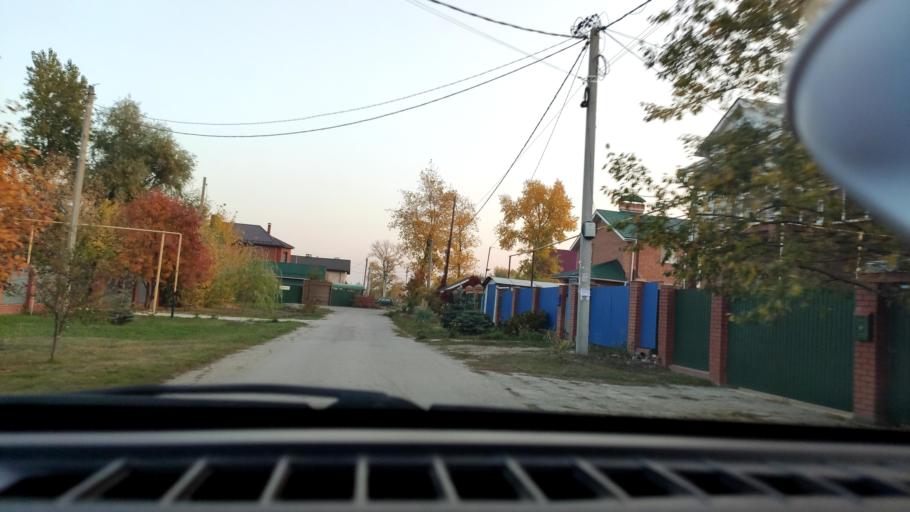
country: RU
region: Samara
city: Samara
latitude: 53.1503
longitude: 50.0860
